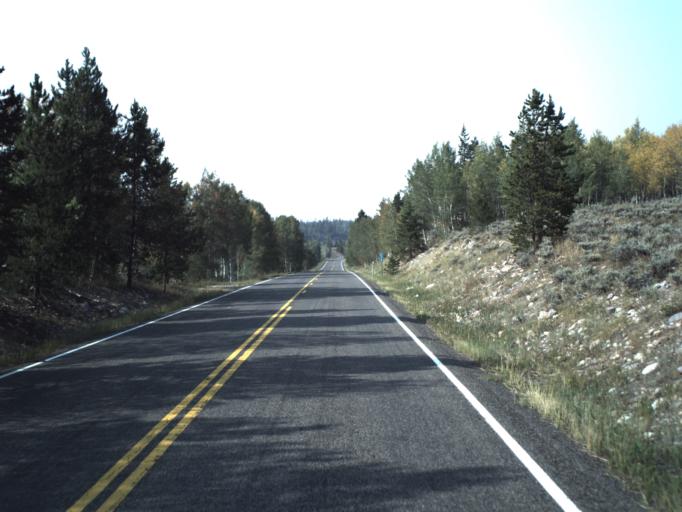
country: US
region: Wyoming
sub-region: Uinta County
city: Evanston
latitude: 40.9048
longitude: -110.8290
